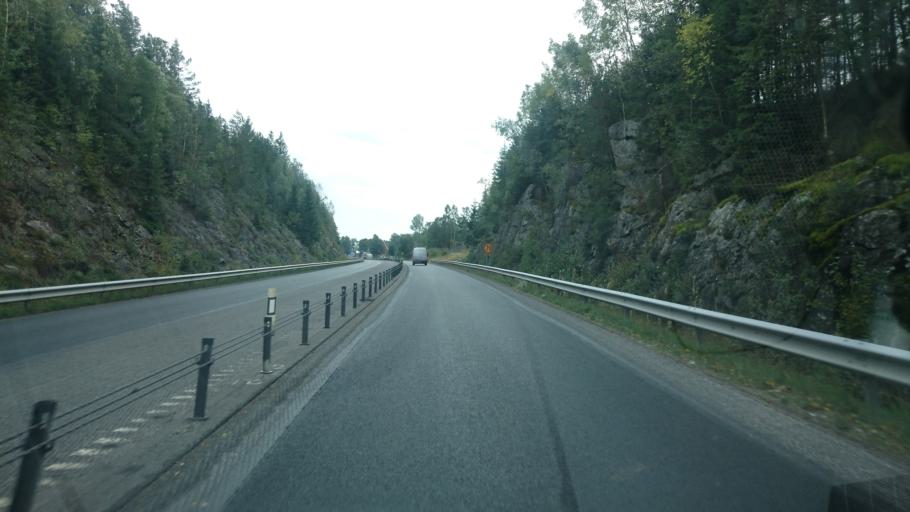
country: SE
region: Vaestra Goetaland
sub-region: Boras Kommun
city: Dalsjofors
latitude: 57.6203
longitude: 13.1048
